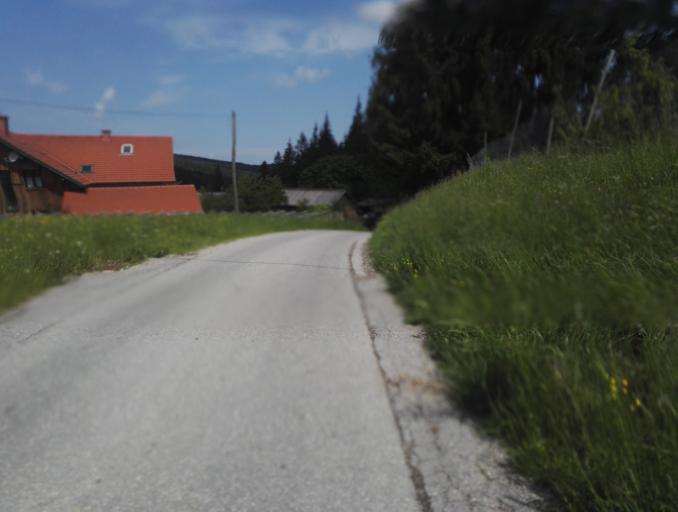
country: AT
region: Styria
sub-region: Politischer Bezirk Graz-Umgebung
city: Sankt Radegund bei Graz
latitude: 47.2115
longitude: 15.4550
